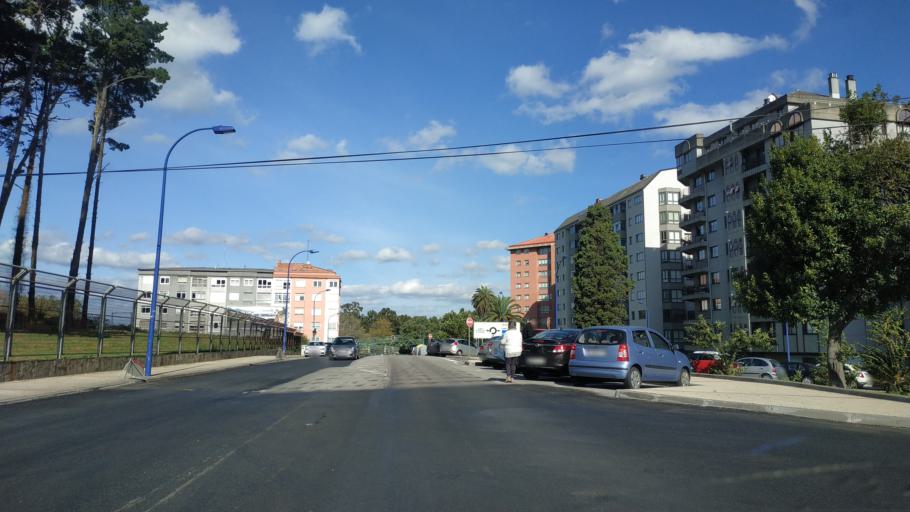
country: ES
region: Galicia
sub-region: Provincia da Coruna
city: Culleredo
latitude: 43.3171
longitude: -8.3732
